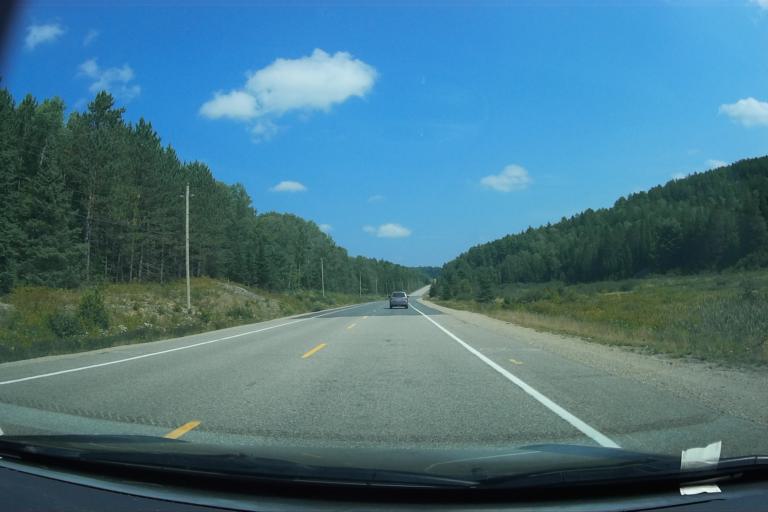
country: CA
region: Ontario
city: Bancroft
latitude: 45.5727
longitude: -78.4275
